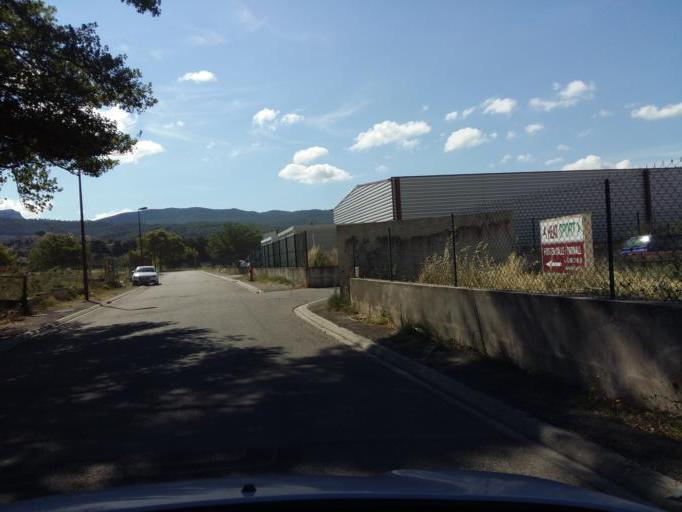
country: FR
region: Provence-Alpes-Cote d'Azur
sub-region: Departement du Vaucluse
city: Sablet
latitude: 44.1953
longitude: 4.9960
